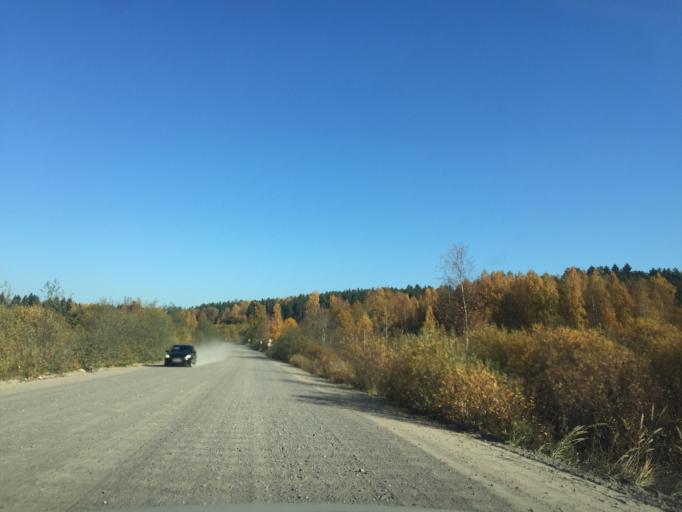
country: RU
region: Leningrad
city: Kuznechnoye
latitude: 61.3102
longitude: 29.9375
